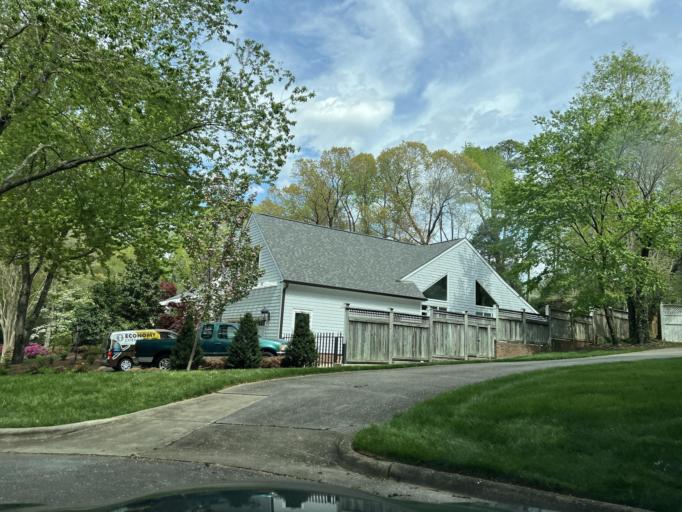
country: US
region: North Carolina
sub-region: Wake County
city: West Raleigh
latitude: 35.8829
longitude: -78.6248
